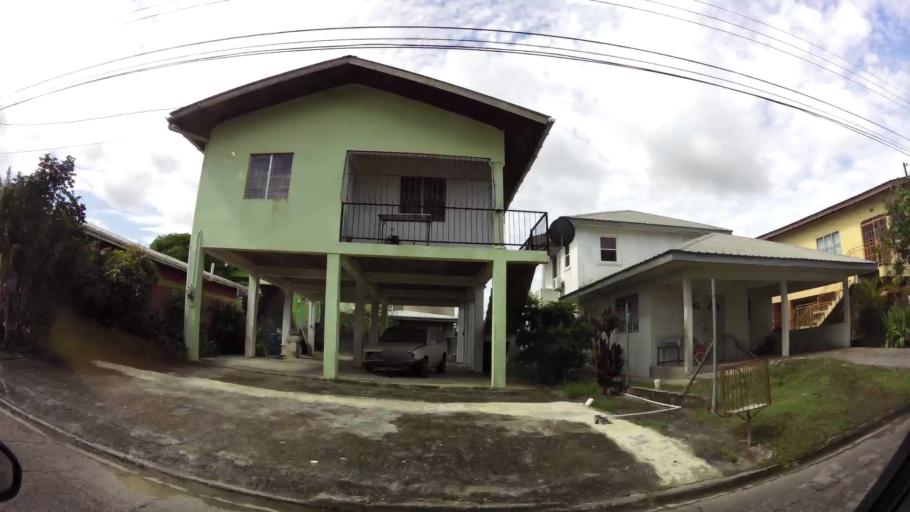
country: TT
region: Chaguanas
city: Chaguanas
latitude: 10.5107
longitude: -61.3927
